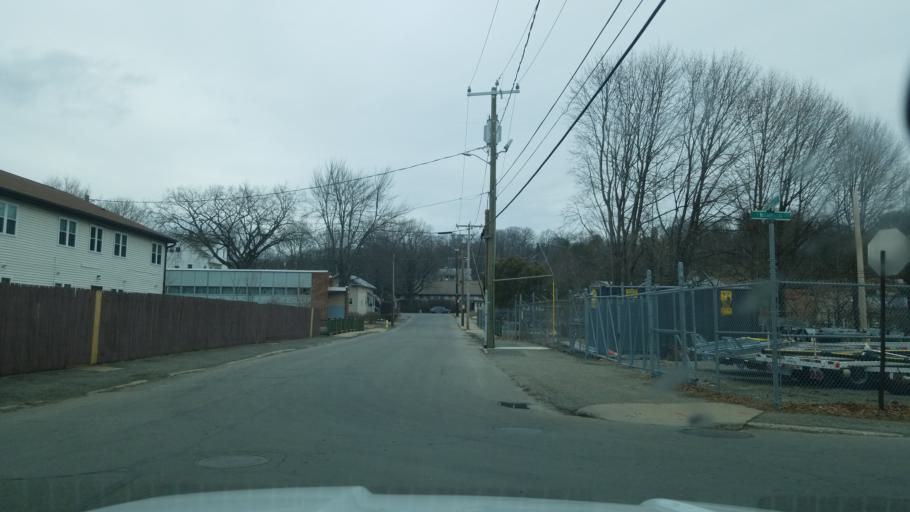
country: US
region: Connecticut
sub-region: Litchfield County
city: Torrington
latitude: 41.8004
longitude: -73.1174
